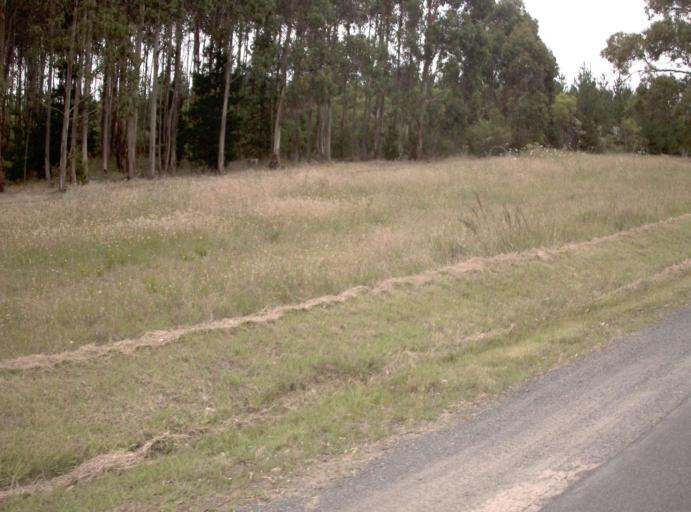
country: AU
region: Victoria
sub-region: Latrobe
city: Moe
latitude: -38.2951
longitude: 146.2889
